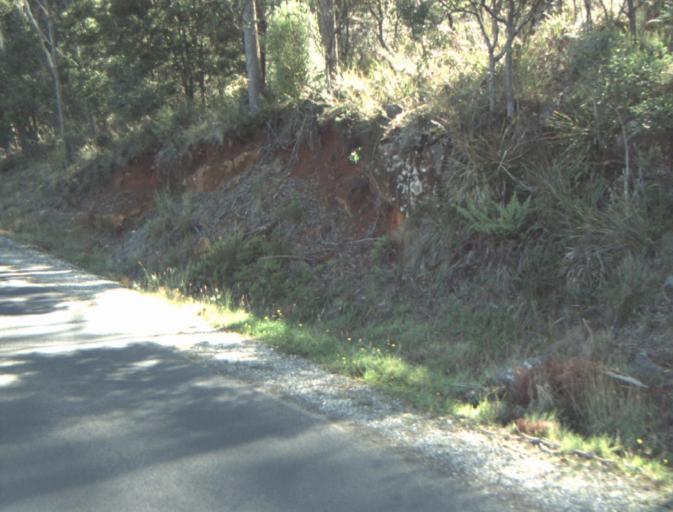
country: AU
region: Tasmania
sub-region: Launceston
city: Mayfield
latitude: -41.3357
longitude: 147.1773
